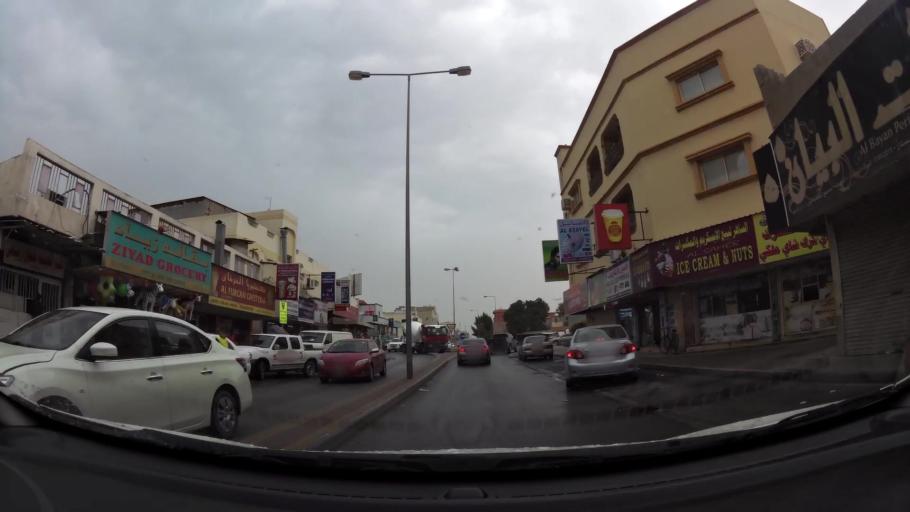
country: BH
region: Northern
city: Madinat `Isa
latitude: 26.1675
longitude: 50.5679
